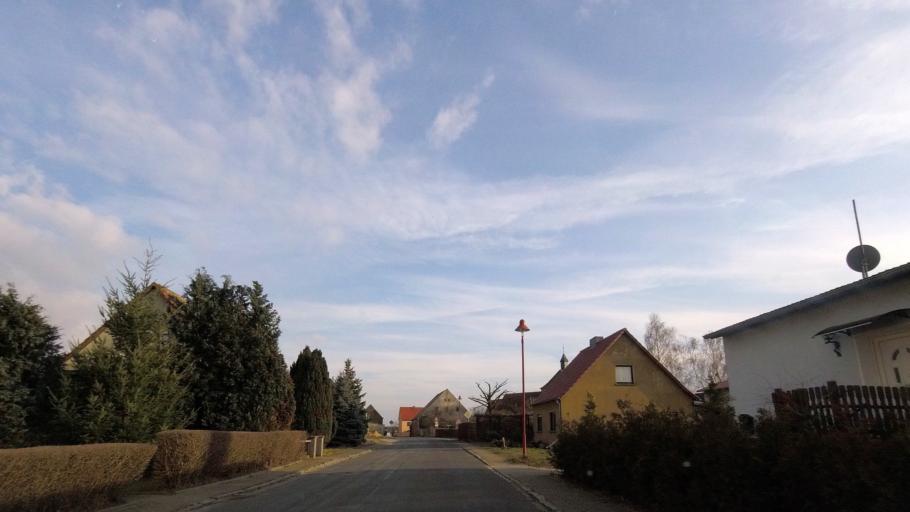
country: DE
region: Brandenburg
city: Belzig
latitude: 52.1032
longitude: 12.5522
